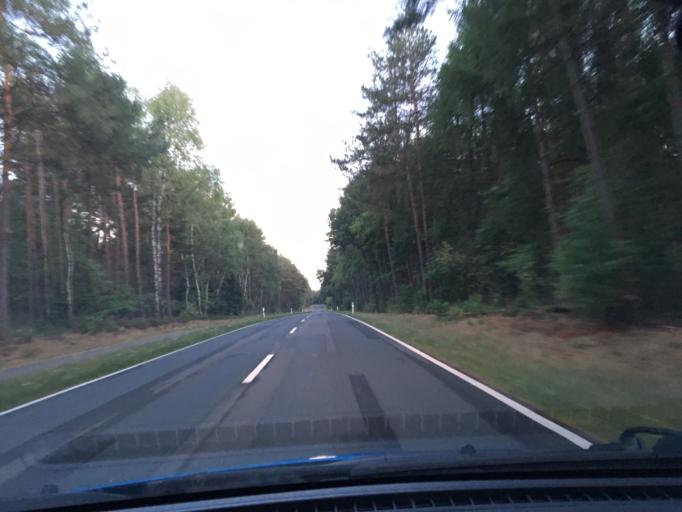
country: DE
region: Lower Saxony
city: Fassberg
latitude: 52.9106
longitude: 10.1515
